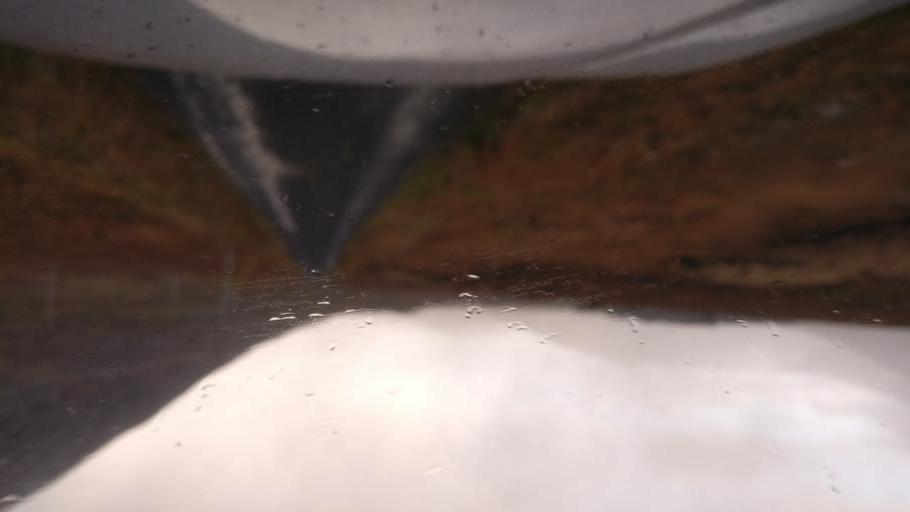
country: IE
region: Connaught
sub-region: County Galway
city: Clifden
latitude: 53.5169
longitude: -9.7185
